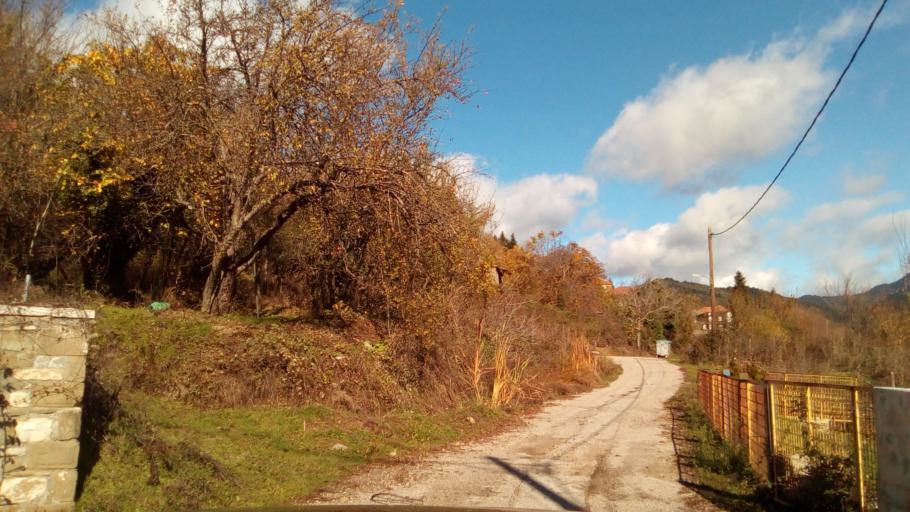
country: GR
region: West Greece
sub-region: Nomos Aitolias kai Akarnanias
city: Nafpaktos
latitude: 38.5922
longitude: 21.9255
